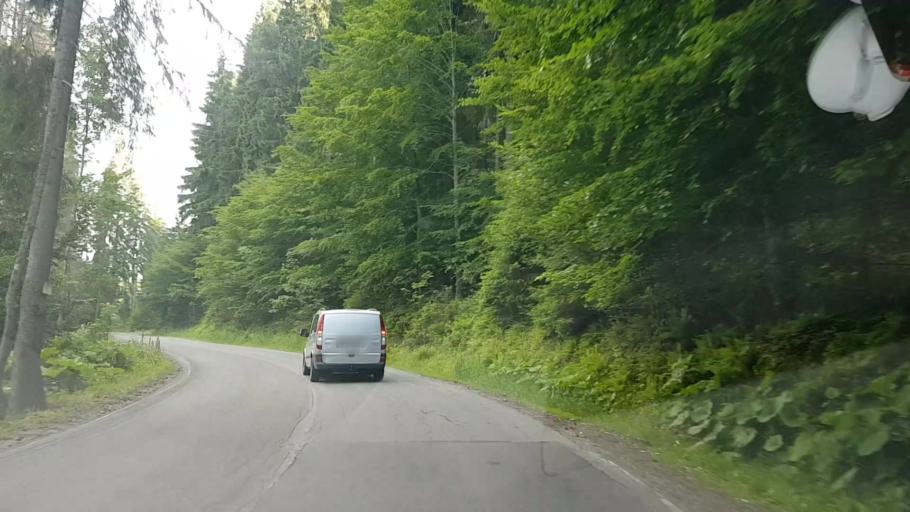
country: RO
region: Harghita
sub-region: Comuna Varsag
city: Varsag
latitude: 46.6677
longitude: 25.3189
